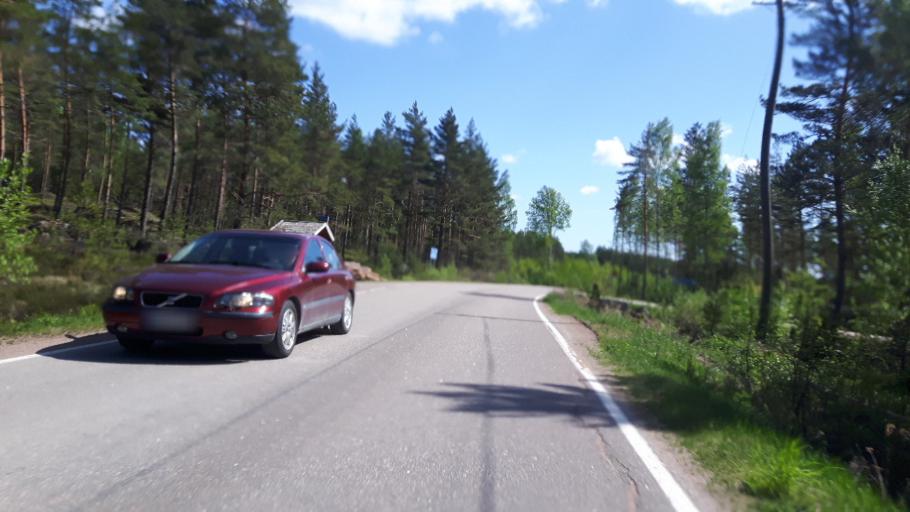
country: FI
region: Kymenlaakso
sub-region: Kotka-Hamina
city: Hamina
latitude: 60.5138
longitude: 27.4229
